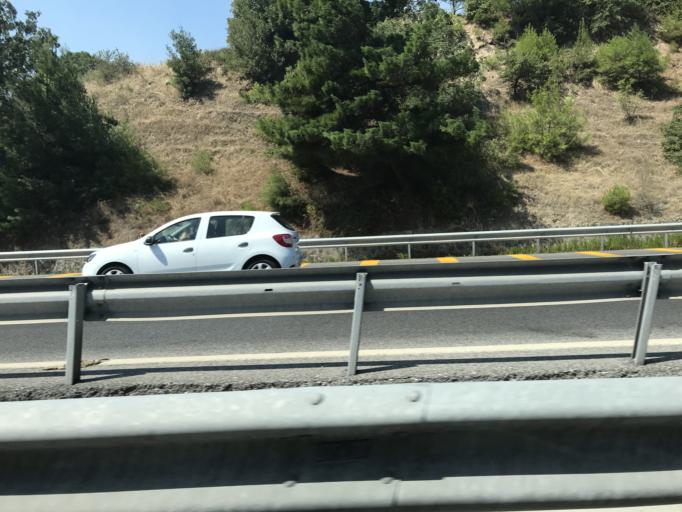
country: TR
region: Izmir
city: Bornova
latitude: 38.5192
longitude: 27.2775
